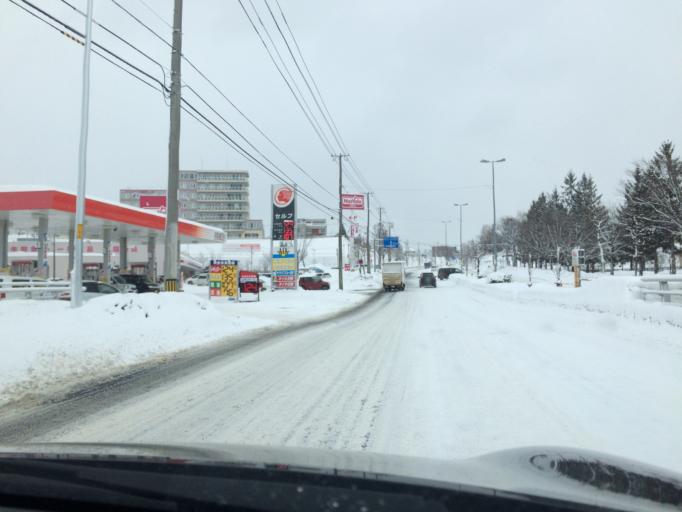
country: JP
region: Hokkaido
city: Ebetsu
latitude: 43.0385
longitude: 141.4827
